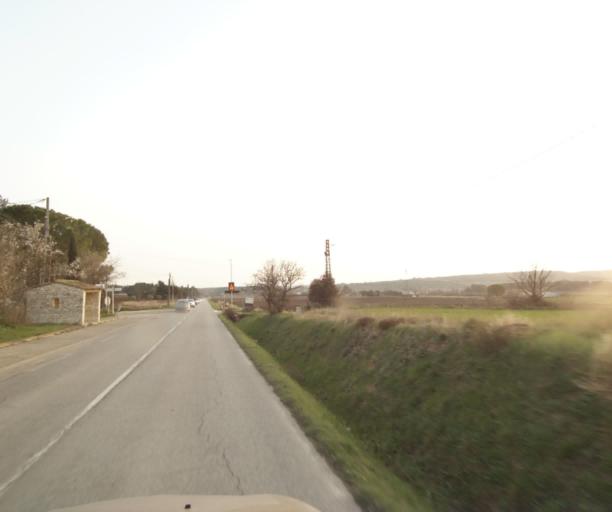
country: FR
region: Provence-Alpes-Cote d'Azur
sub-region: Departement des Bouches-du-Rhone
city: Eguilles
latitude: 43.5509
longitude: 5.3495
